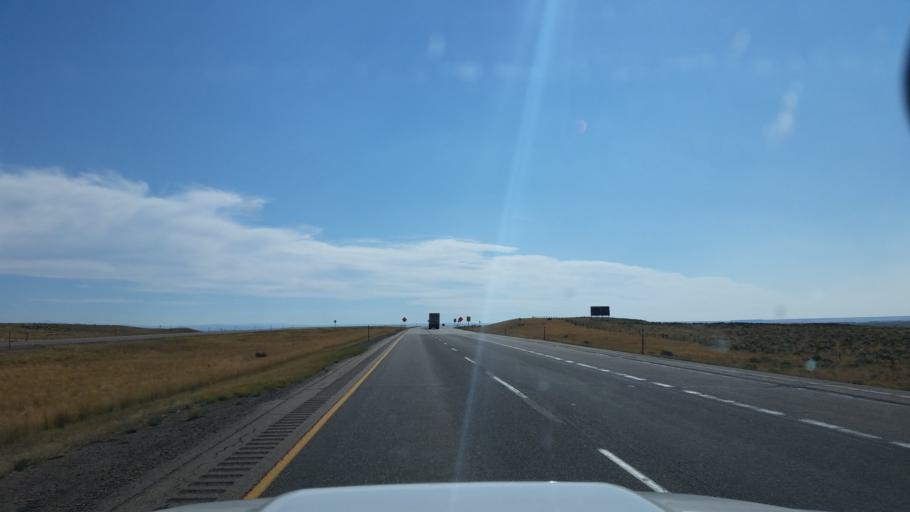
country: US
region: Wyoming
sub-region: Uinta County
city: Lyman
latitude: 41.3963
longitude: -110.1772
